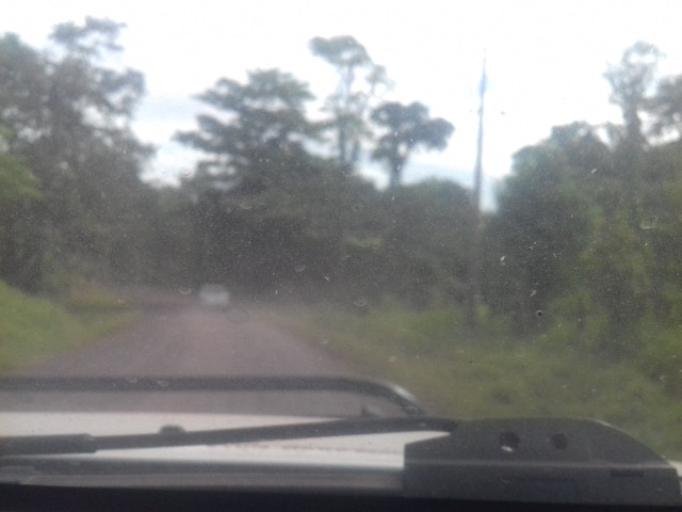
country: NI
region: Atlantico Norte (RAAN)
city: Waslala
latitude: 13.4324
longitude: -85.3114
